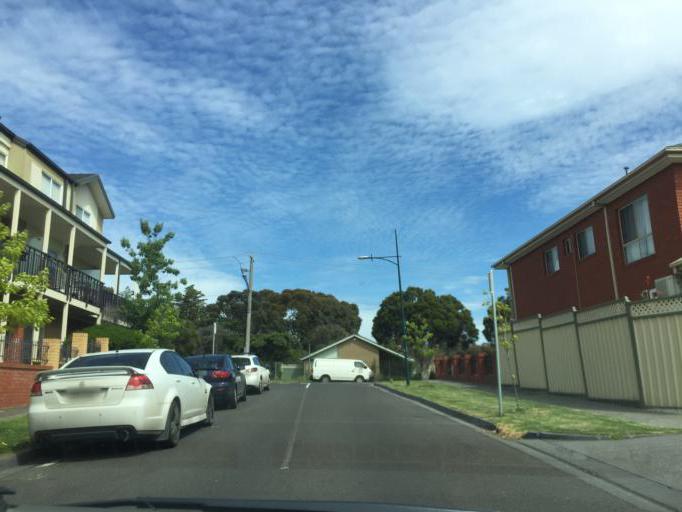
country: AU
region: Victoria
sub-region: Maribyrnong
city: Maidstone
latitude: -37.7744
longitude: 144.8795
